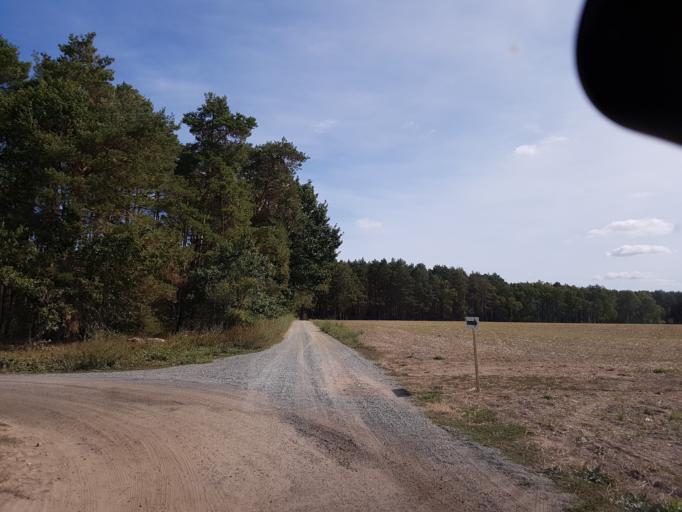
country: DE
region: Brandenburg
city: Sonnewalde
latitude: 51.7562
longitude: 13.6322
